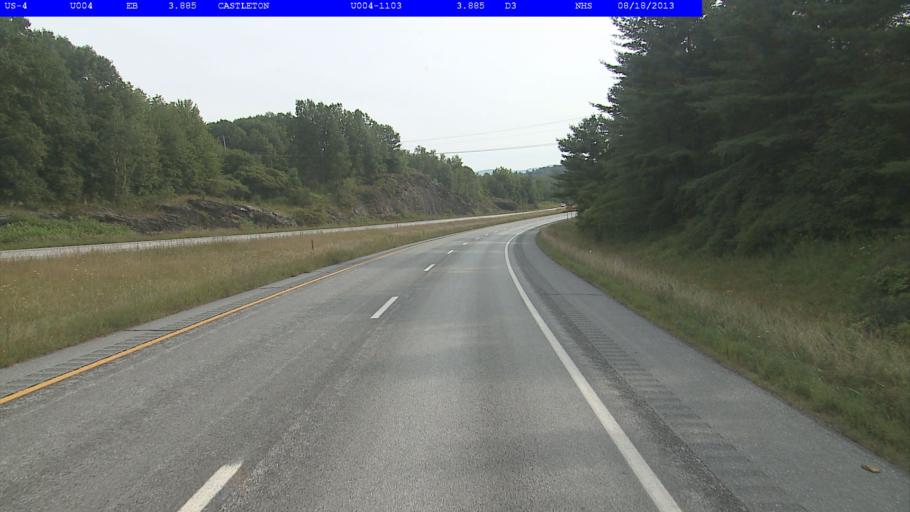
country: US
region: Vermont
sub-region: Rutland County
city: Fair Haven
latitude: 43.6100
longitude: -73.2366
